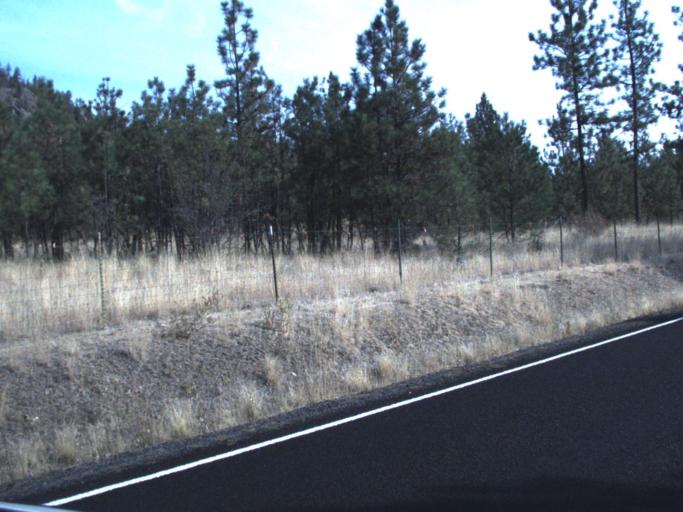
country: US
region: Washington
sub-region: Spokane County
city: Fairchild Air Force Base
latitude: 47.8440
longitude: -117.7348
